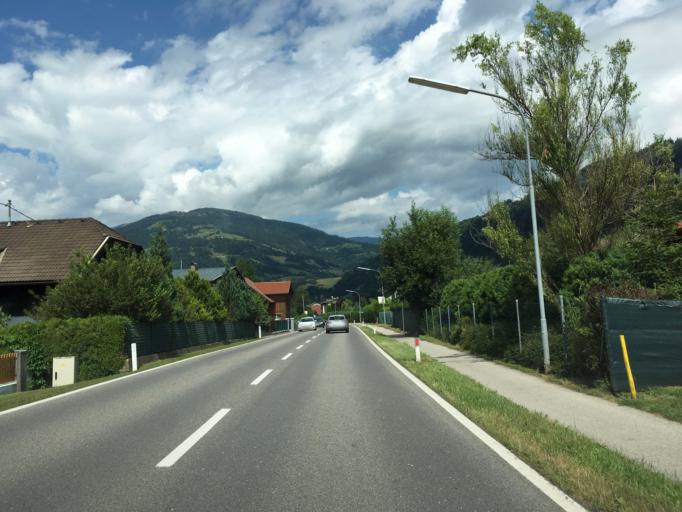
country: AT
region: Carinthia
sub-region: Politischer Bezirk Spittal an der Drau
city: Radenthein
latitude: 46.7893
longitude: 13.7299
